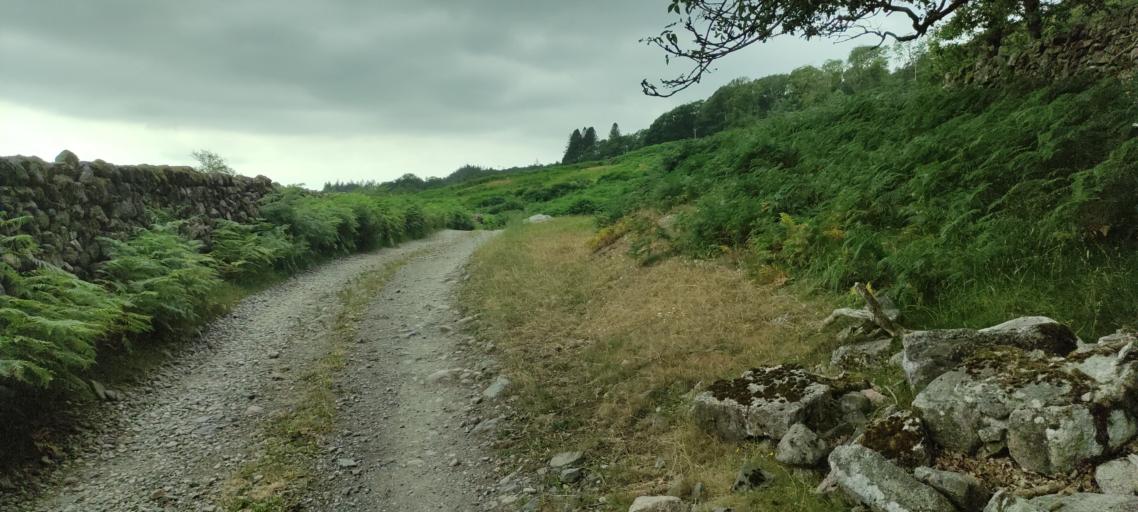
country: GB
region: England
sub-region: Cumbria
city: Seascale
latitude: 54.4023
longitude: -3.3101
